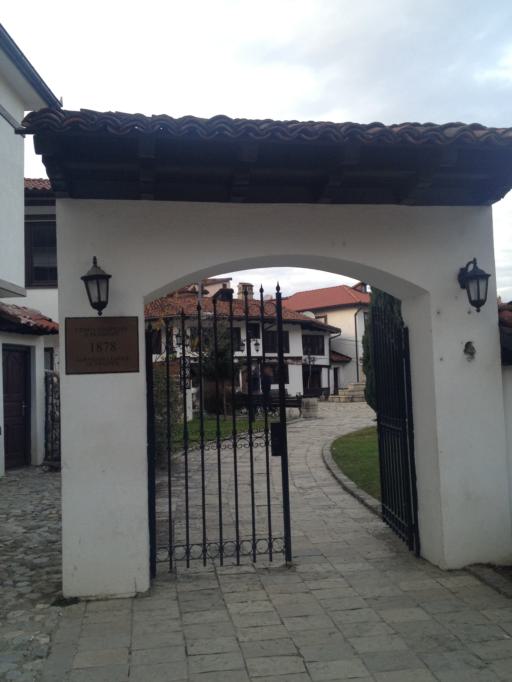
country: XK
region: Prizren
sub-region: Prizren
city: Prizren
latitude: 42.2113
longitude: 20.7437
